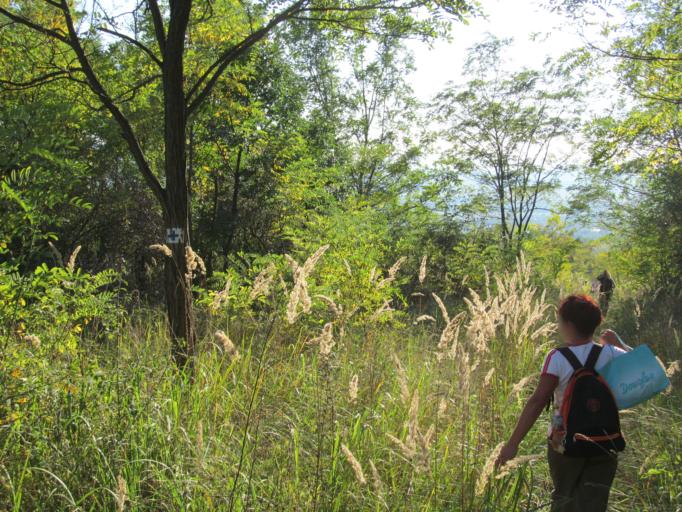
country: HU
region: Pest
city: Szob
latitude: 47.8934
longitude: 18.8004
